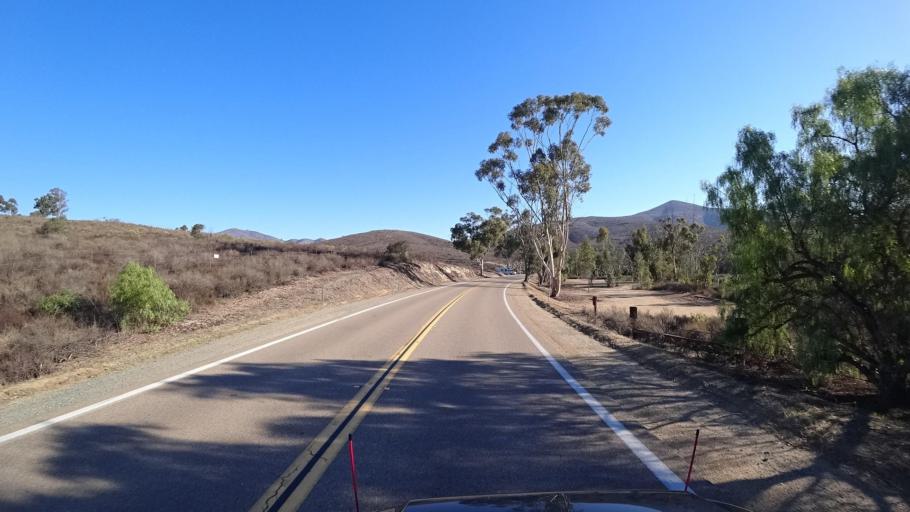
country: US
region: California
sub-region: San Diego County
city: La Presa
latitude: 32.6460
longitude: -116.9322
